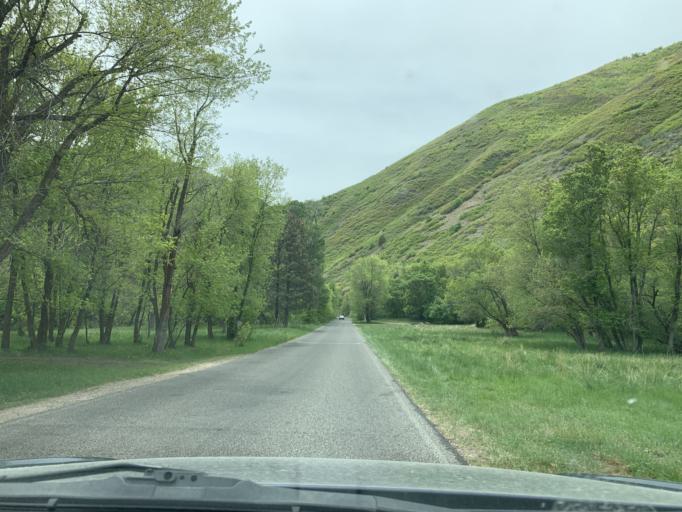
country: US
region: Utah
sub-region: Utah County
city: Mapleton
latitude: 40.1784
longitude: -111.4716
